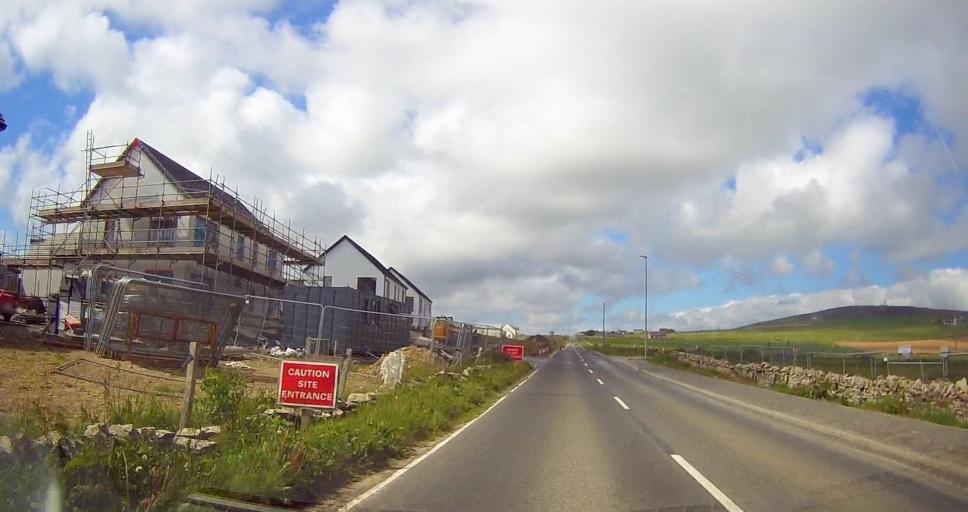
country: GB
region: Scotland
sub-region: Orkney Islands
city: Orkney
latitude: 58.9775
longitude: -2.9848
